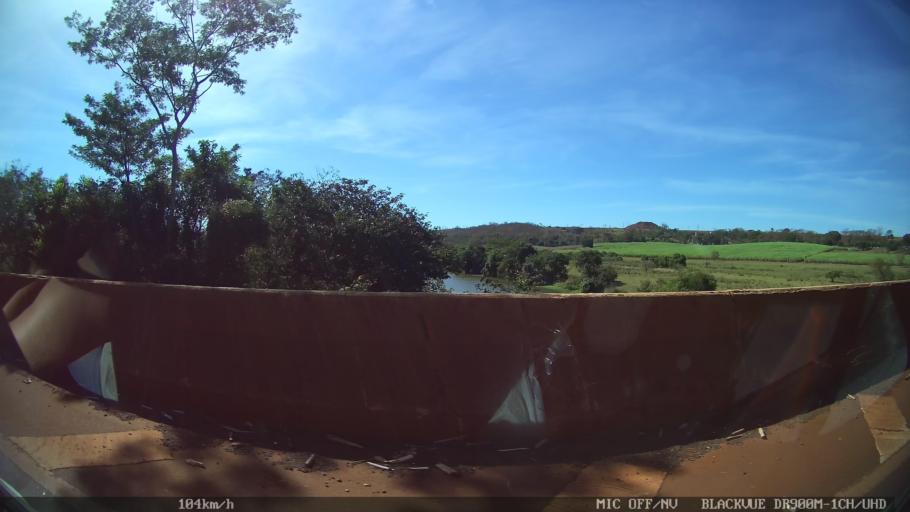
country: BR
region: Sao Paulo
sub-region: Sao Joaquim Da Barra
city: Sao Joaquim da Barra
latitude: -20.5313
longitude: -47.8313
